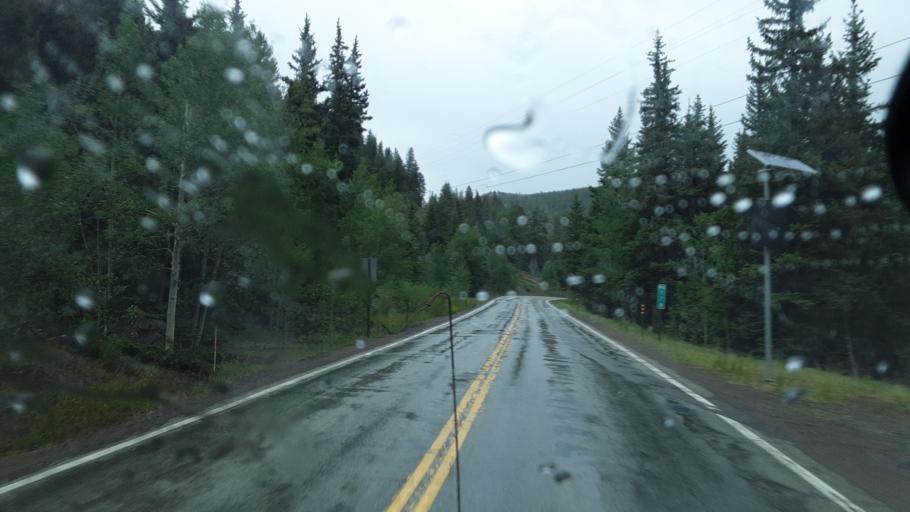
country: US
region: Colorado
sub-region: Mineral County
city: Creede
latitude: 37.5870
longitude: -106.7349
